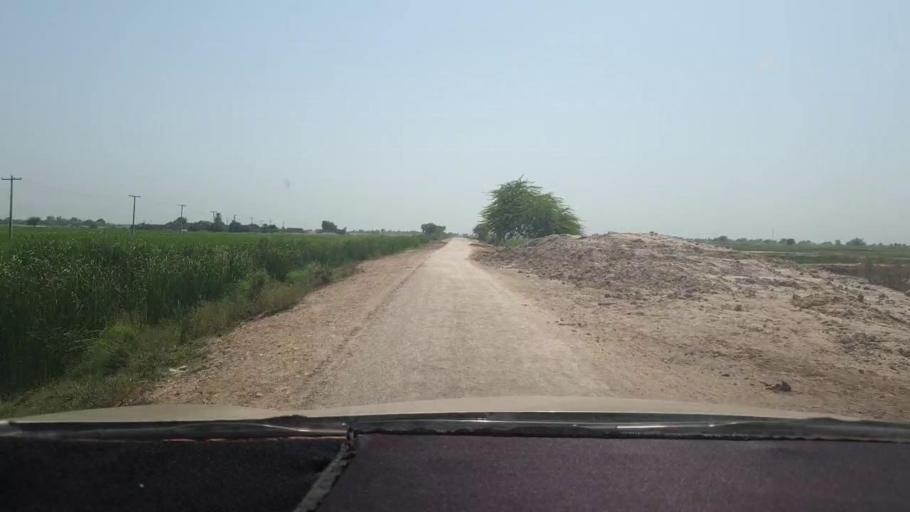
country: PK
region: Sindh
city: Miro Khan
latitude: 27.6792
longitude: 68.0958
